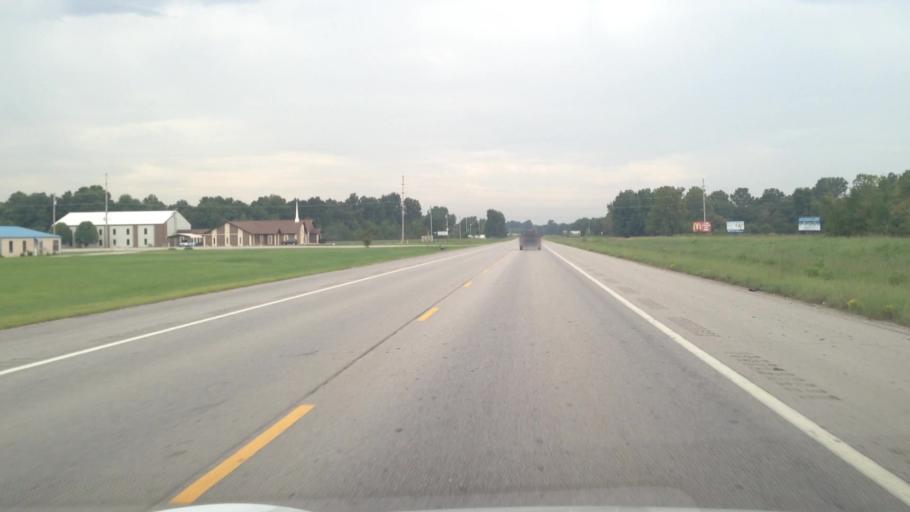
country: US
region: Kansas
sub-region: Cherokee County
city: Baxter Springs
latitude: 37.0695
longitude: -94.7229
